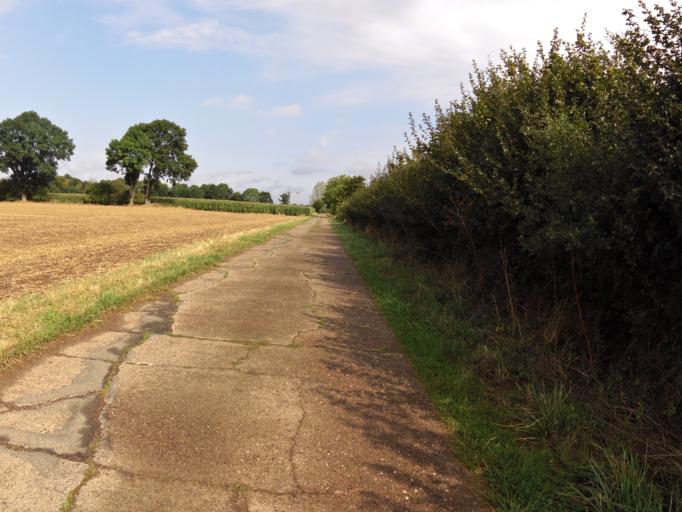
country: DE
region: Lower Saxony
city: Drakenburg
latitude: 52.7015
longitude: 9.1921
